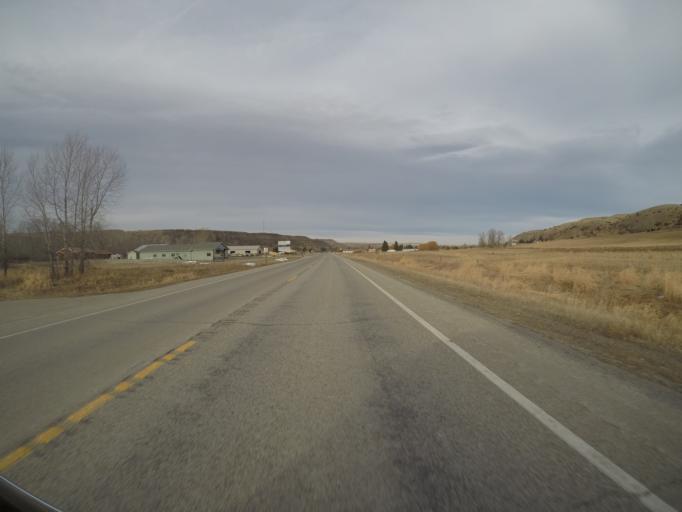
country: US
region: Montana
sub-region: Stillwater County
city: Absarokee
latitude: 45.5078
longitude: -109.4486
